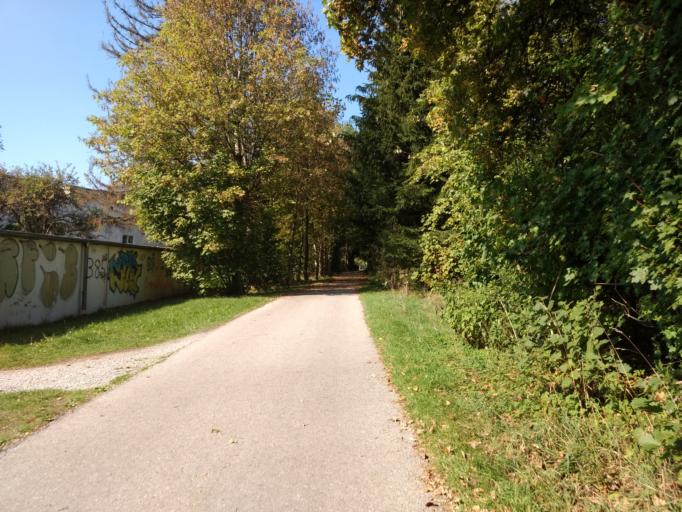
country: DE
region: Bavaria
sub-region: Upper Bavaria
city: Geretsried
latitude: 47.8471
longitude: 11.4792
